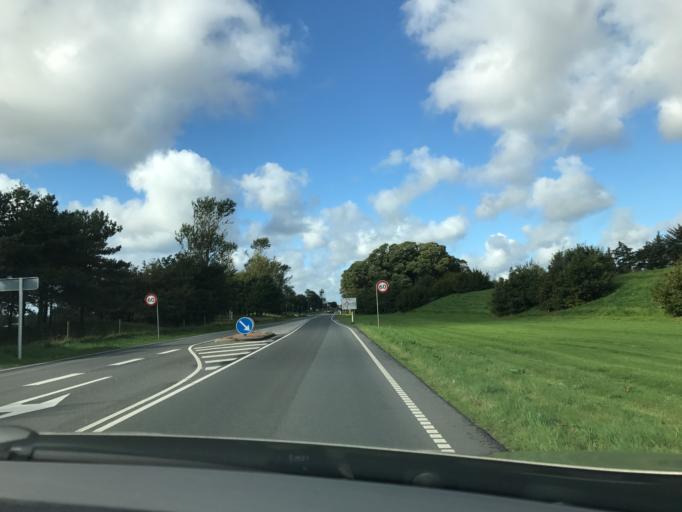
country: DK
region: South Denmark
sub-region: Billund Kommune
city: Billund
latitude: 55.7243
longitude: 9.1380
